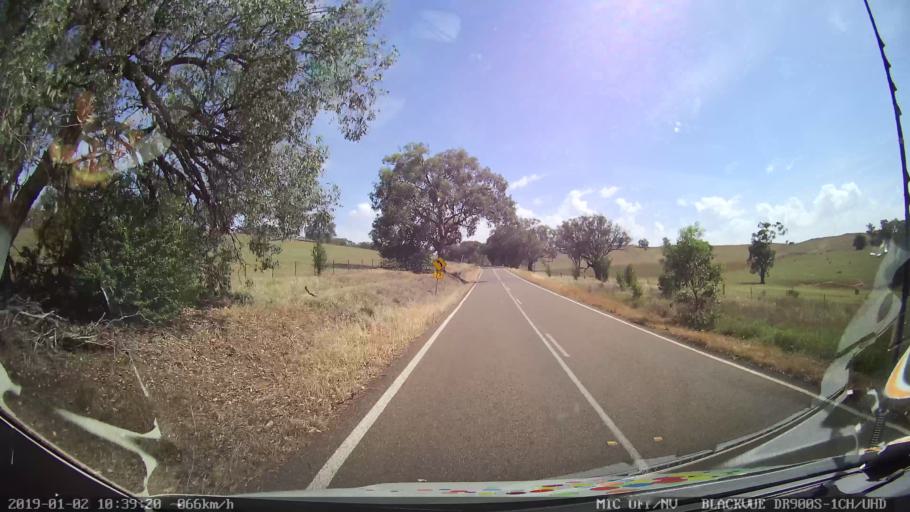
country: AU
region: New South Wales
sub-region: Gundagai
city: Gundagai
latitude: -34.8119
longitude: 148.3194
